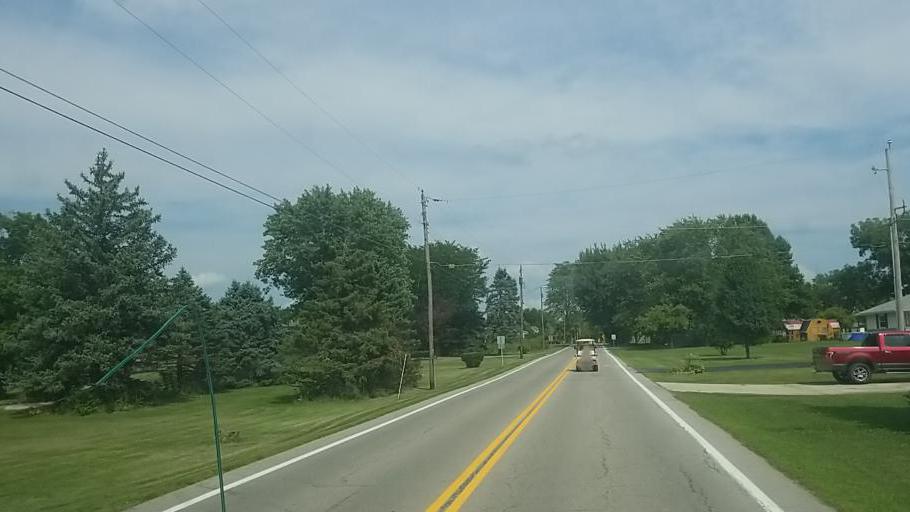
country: US
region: Ohio
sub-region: Hardin County
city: Forest
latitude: 40.8036
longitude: -83.5190
